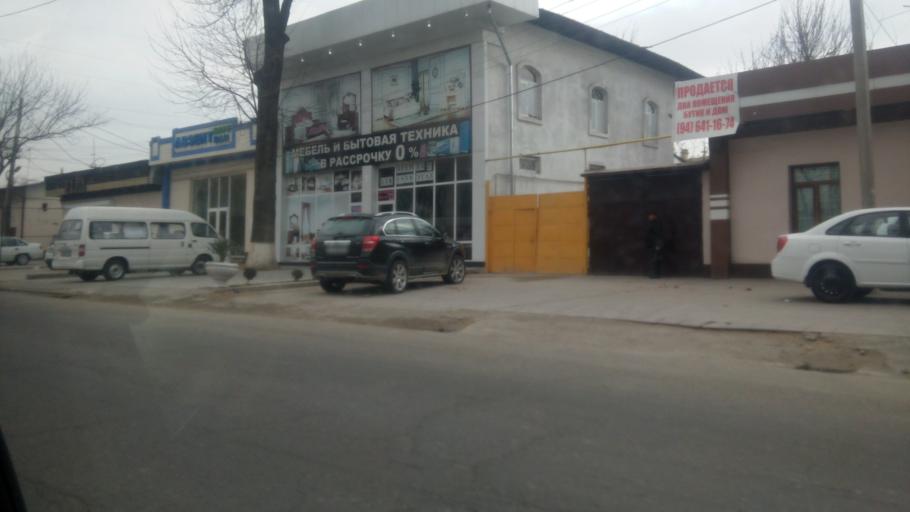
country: UZ
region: Toshkent Shahri
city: Tashkent
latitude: 41.3491
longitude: 69.2305
